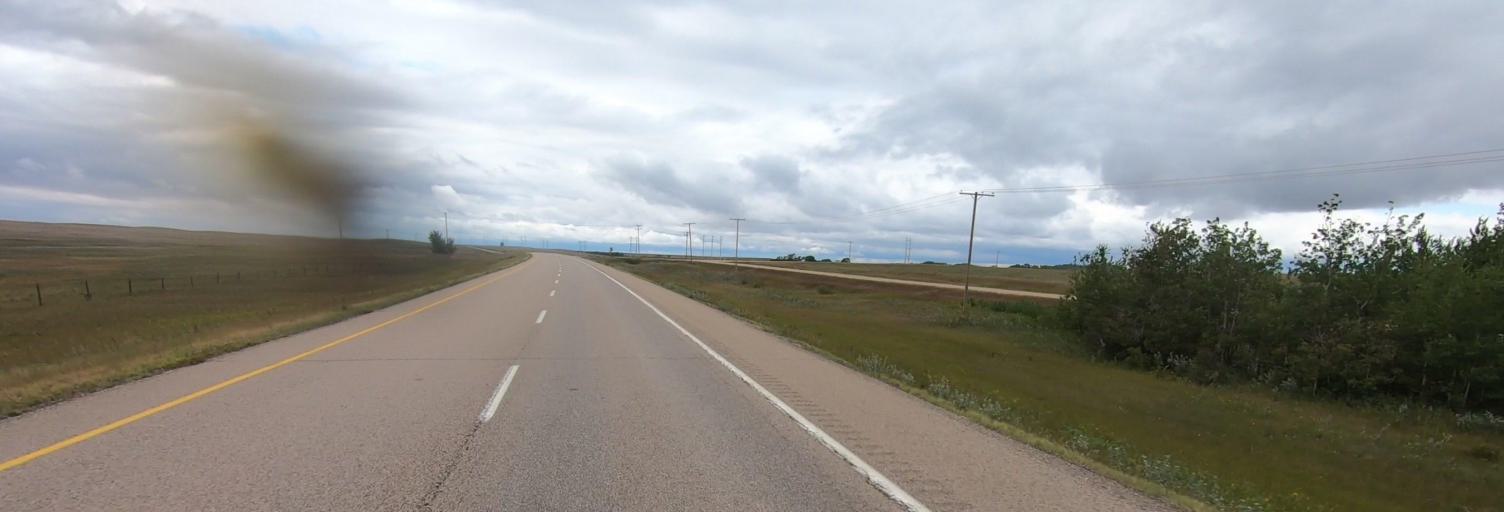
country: CA
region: Saskatchewan
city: Gravelbourg
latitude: 50.4775
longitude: -106.7809
